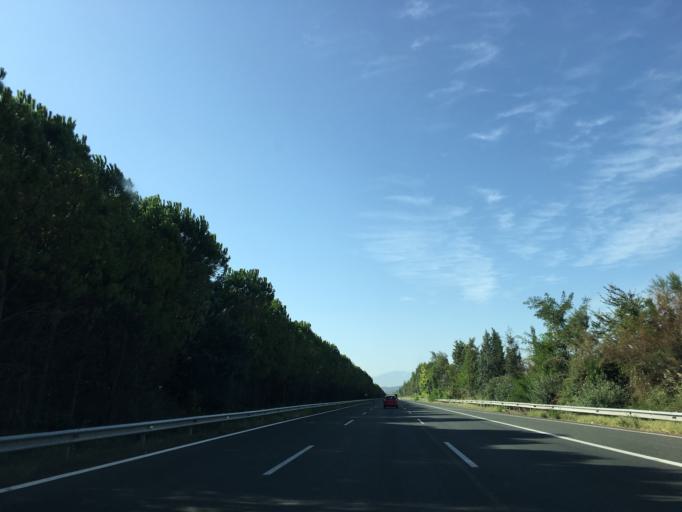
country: GR
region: Central Macedonia
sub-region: Nomos Pierias
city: Aiginio
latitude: 40.5105
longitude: 22.5692
